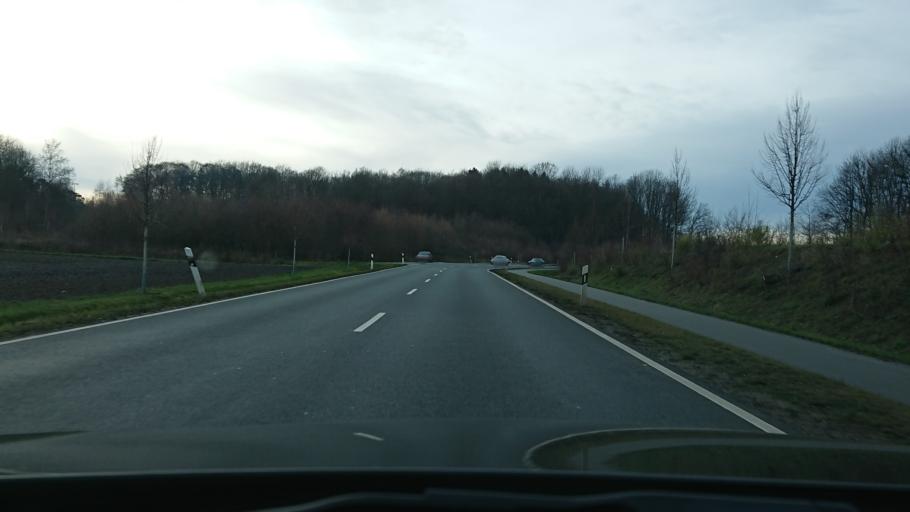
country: DE
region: North Rhine-Westphalia
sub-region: Regierungsbezirk Koln
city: Frechen
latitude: 50.9212
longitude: 6.7995
